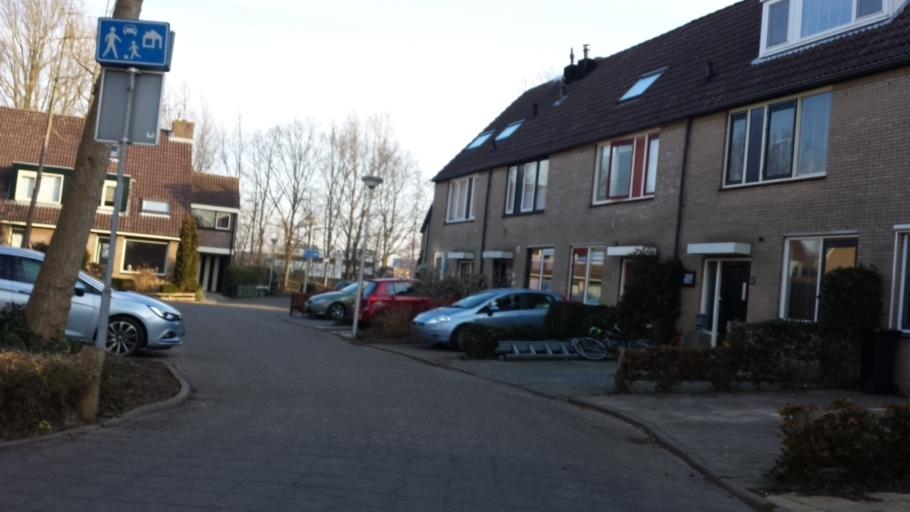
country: NL
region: South Holland
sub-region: Bodegraven-Reeuwijk
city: Reeuwijk
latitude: 52.0378
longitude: 4.7142
